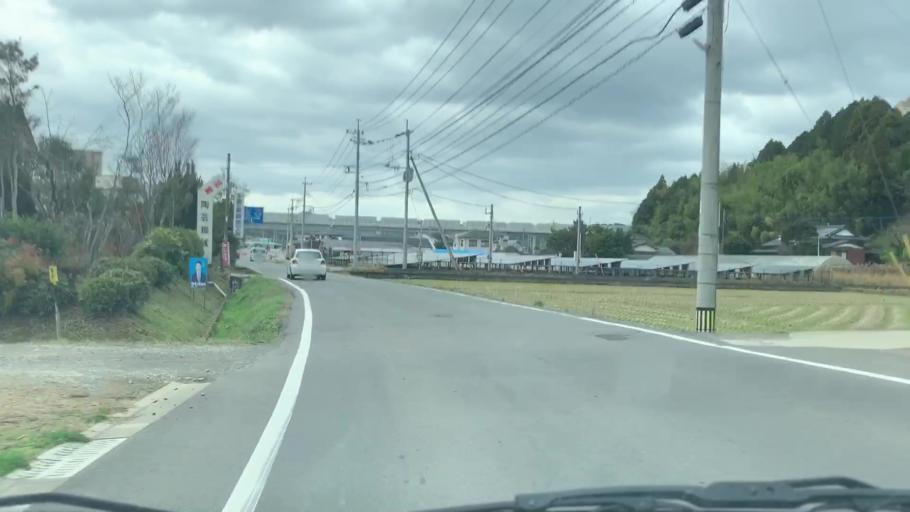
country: JP
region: Saga Prefecture
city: Ureshinomachi-shimojuku
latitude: 33.1290
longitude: 129.9981
